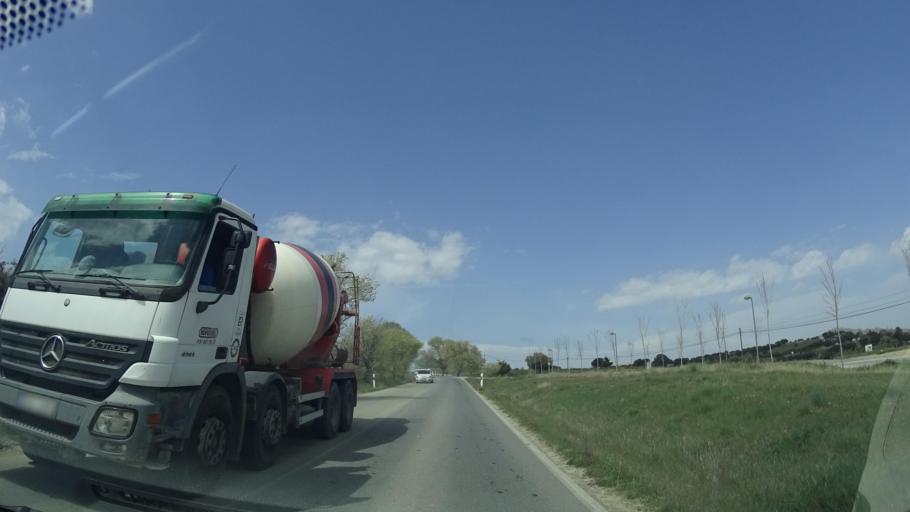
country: ES
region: Madrid
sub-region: Provincia de Madrid
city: Colmenar Viejo
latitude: 40.6834
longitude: -3.7695
